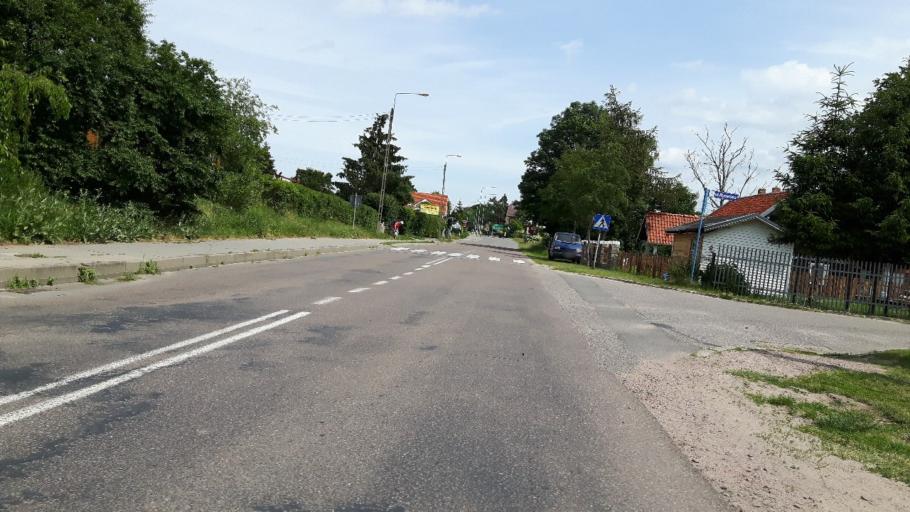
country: PL
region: Pomeranian Voivodeship
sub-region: Powiat nowodworski
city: Stegna
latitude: 54.3269
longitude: 19.1073
